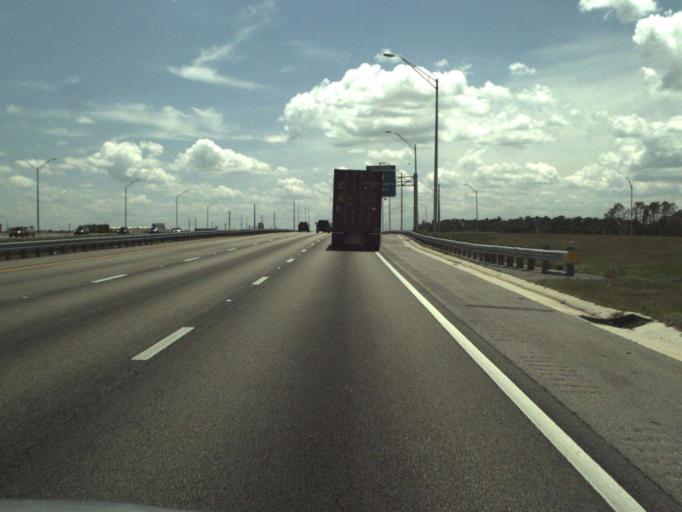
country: US
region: Florida
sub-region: Seminole County
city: Lake Mary
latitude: 28.8142
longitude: -81.3368
